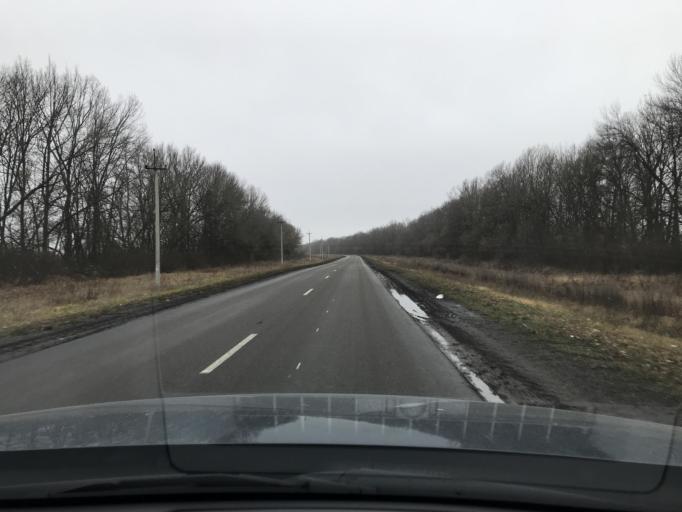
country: RU
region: Penza
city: Zemetchino
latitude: 53.5405
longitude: 42.6663
